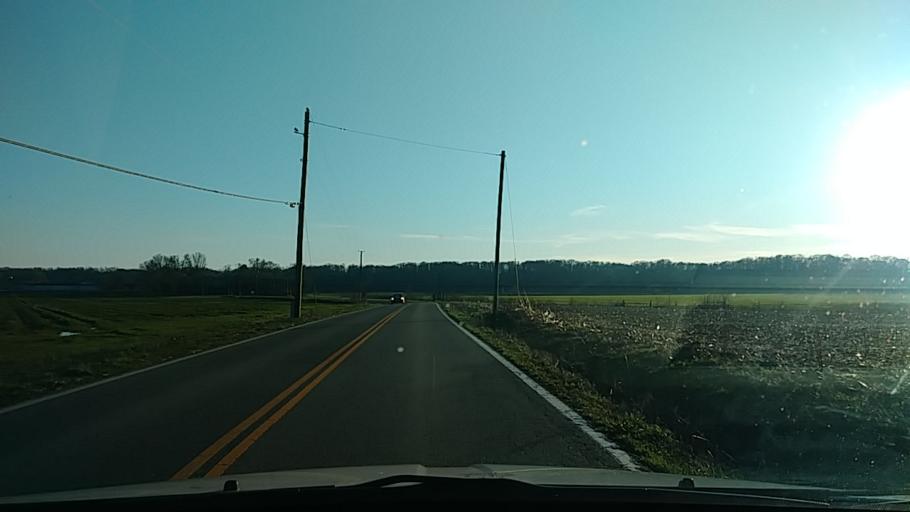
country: US
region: Tennessee
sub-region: Jefferson County
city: White Pine
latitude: 36.1668
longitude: -83.1616
